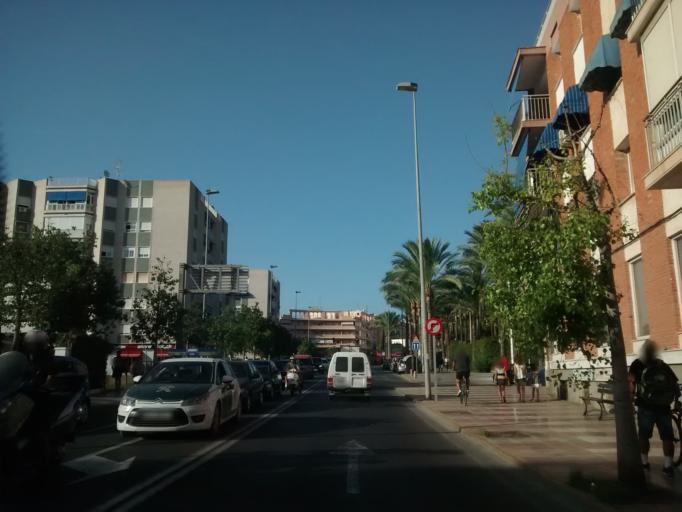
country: ES
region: Valencia
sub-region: Provincia de Alicante
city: Santa Pola
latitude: 38.1946
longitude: -0.5607
